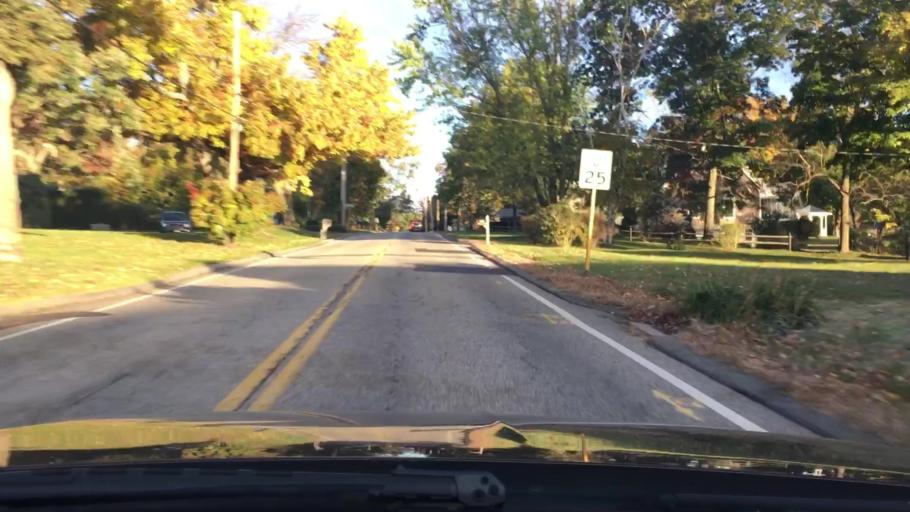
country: US
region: Massachusetts
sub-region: Hampden County
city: East Longmeadow
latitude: 42.0416
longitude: -72.4996
